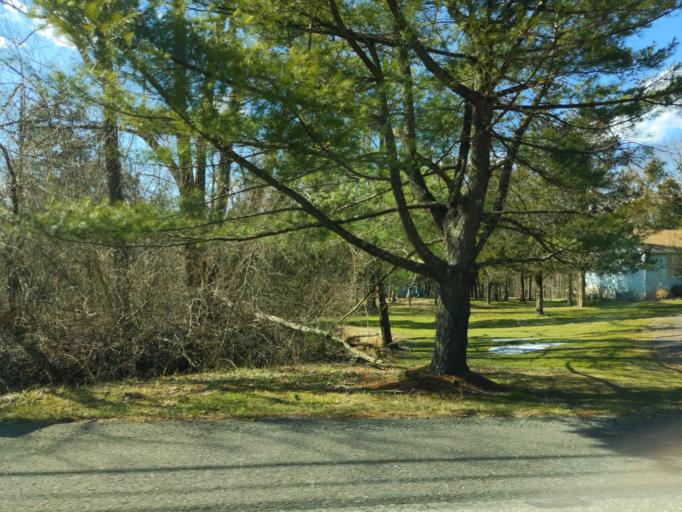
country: US
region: Pennsylvania
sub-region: Montgomery County
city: Red Hill
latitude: 40.3537
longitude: -75.4621
